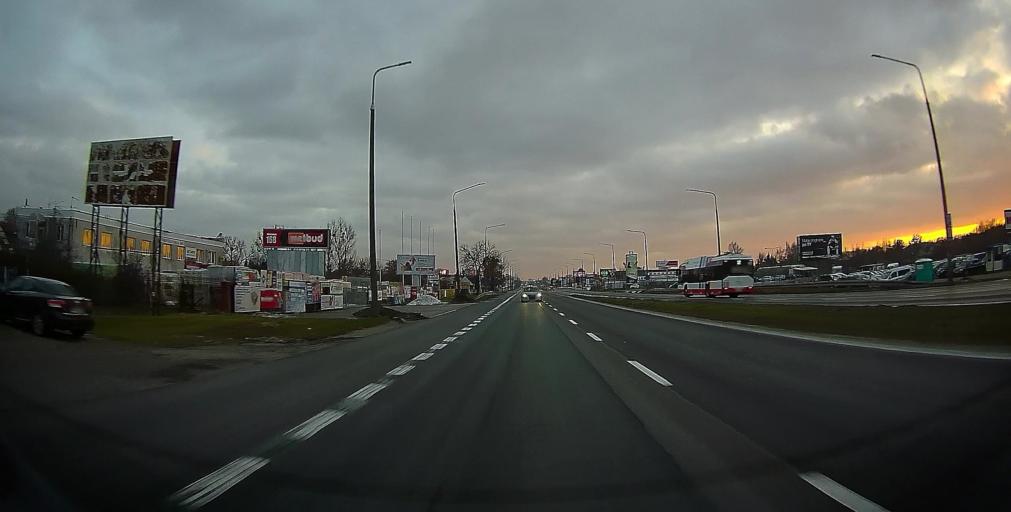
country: PL
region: Masovian Voivodeship
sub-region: Radom
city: Radom
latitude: 51.4404
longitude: 21.1462
